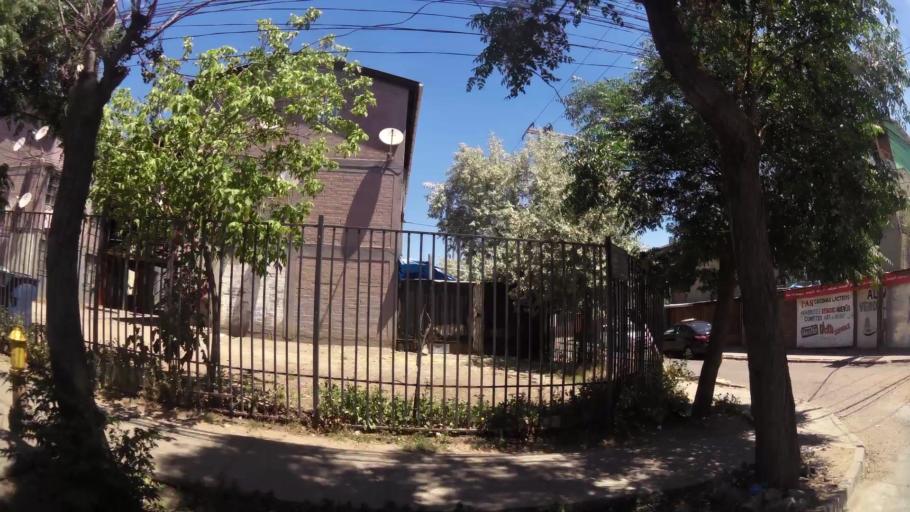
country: CL
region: Santiago Metropolitan
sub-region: Provincia de Maipo
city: San Bernardo
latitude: -33.5987
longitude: -70.6767
